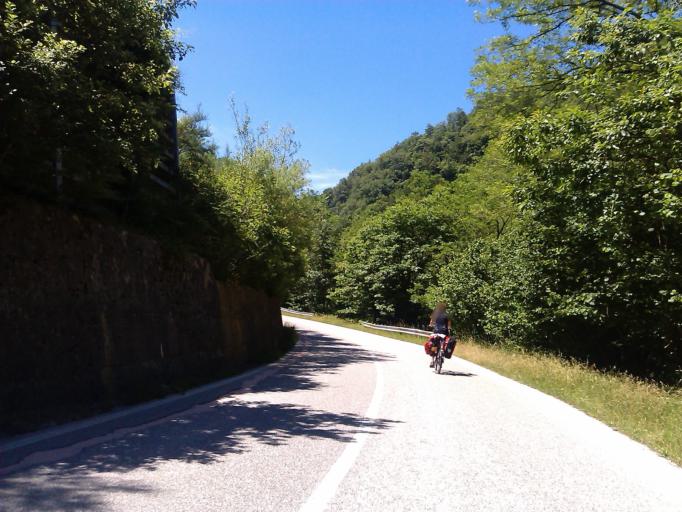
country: IT
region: Tuscany
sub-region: Provincia di Prato
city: Cantagallo
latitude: 44.0464
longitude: 11.0415
